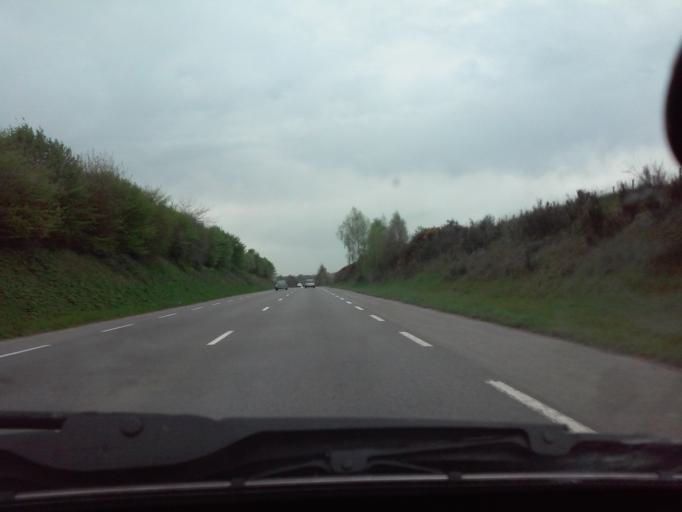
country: FR
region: Brittany
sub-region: Departement d'Ille-et-Vilaine
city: Fougeres
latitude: 48.3366
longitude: -1.1971
